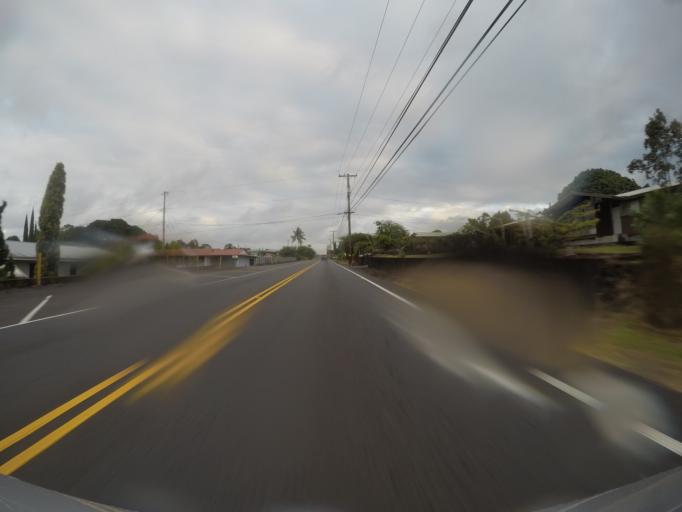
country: US
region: Hawaii
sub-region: Hawaii County
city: Hilo
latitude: 19.6898
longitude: -155.0902
